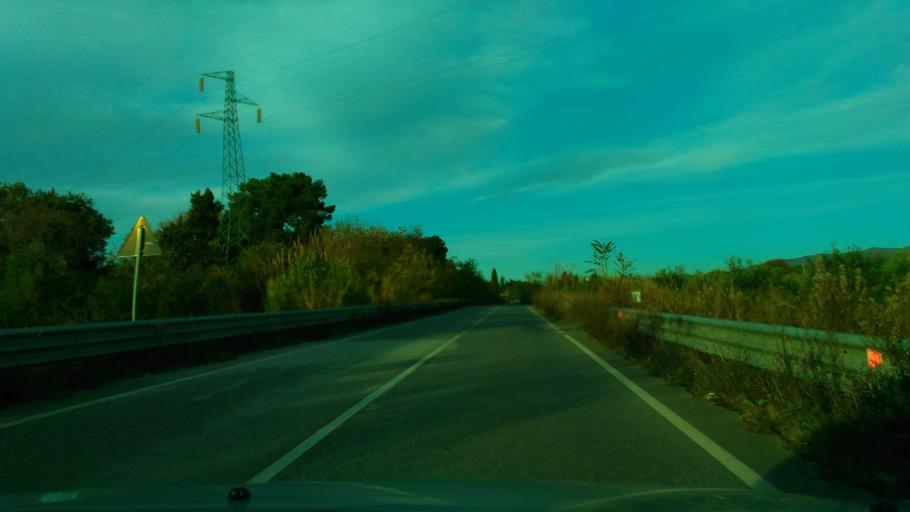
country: IT
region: Tuscany
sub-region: Provincia di Livorno
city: S.P. in Palazzi
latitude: 43.3508
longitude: 10.5049
